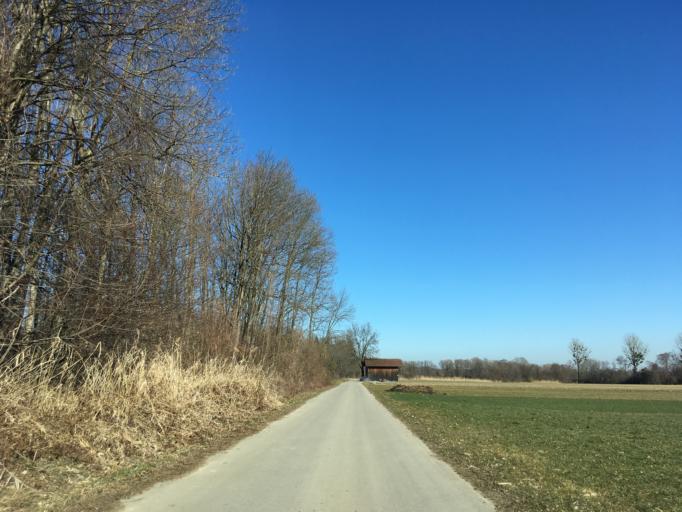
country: DE
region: Bavaria
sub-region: Upper Bavaria
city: Bad Aibling
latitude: 47.8265
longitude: 11.9802
